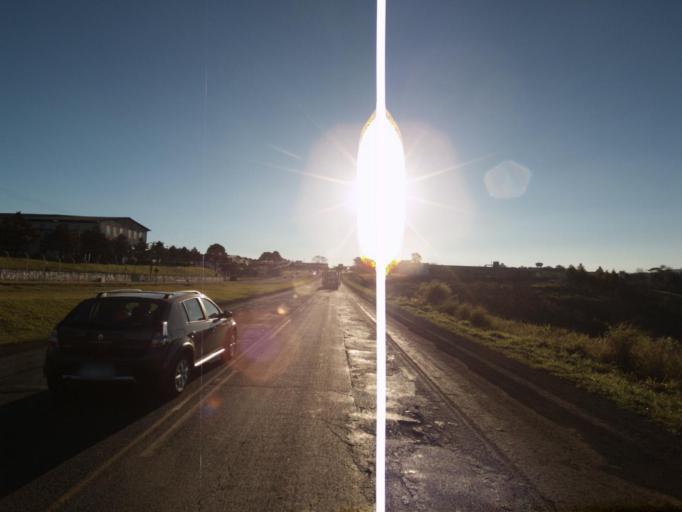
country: BR
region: Santa Catarina
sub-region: Chapeco
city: Chapeco
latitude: -26.8634
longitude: -52.9739
